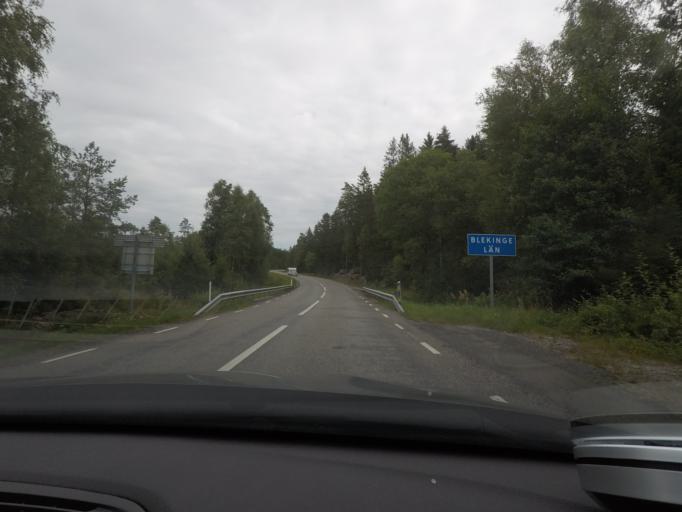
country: SE
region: Blekinge
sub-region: Olofstroms Kommun
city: Olofstroem
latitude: 56.4400
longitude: 14.4972
